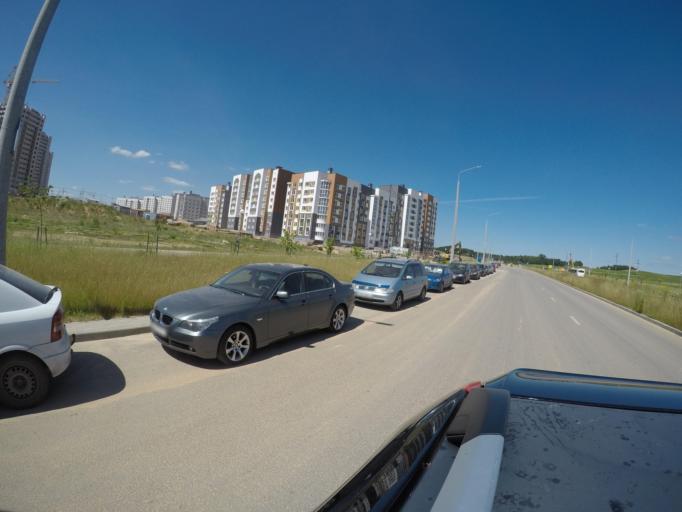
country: BY
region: Grodnenskaya
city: Hrodna
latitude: 53.7218
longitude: 23.8862
